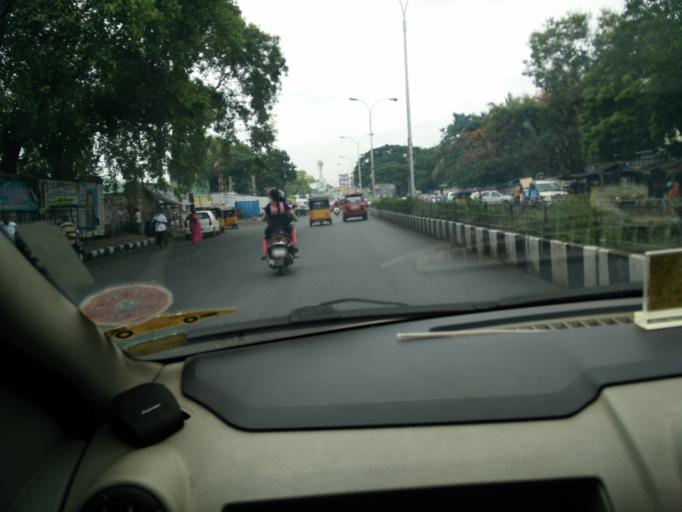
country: IN
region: Tamil Nadu
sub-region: Chennai
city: Chennai
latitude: 13.0754
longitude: 80.2763
